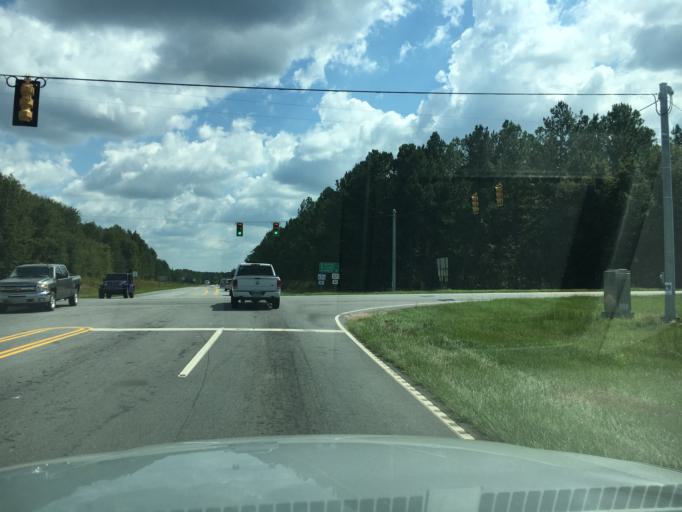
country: US
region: South Carolina
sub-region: Greenwood County
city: Greenwood
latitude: 34.1426
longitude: -82.1490
